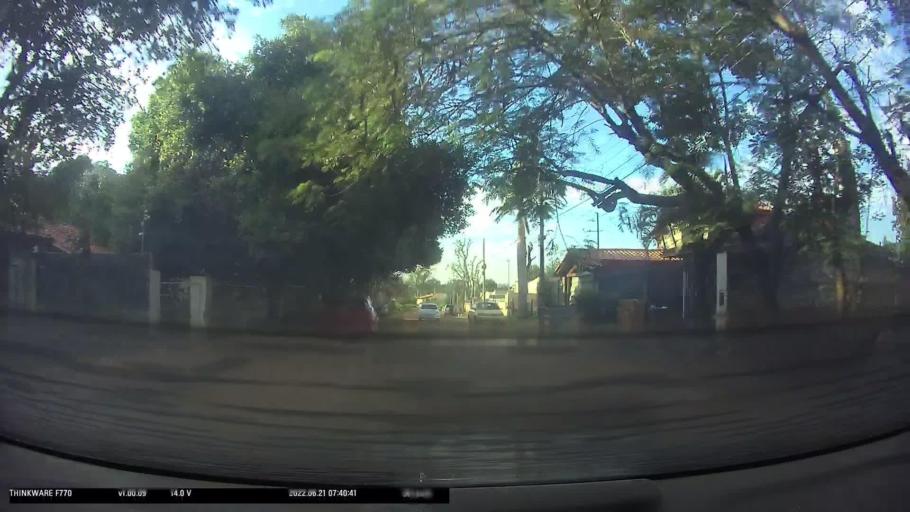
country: PY
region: Central
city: Limpio
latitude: -25.2460
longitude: -57.5074
